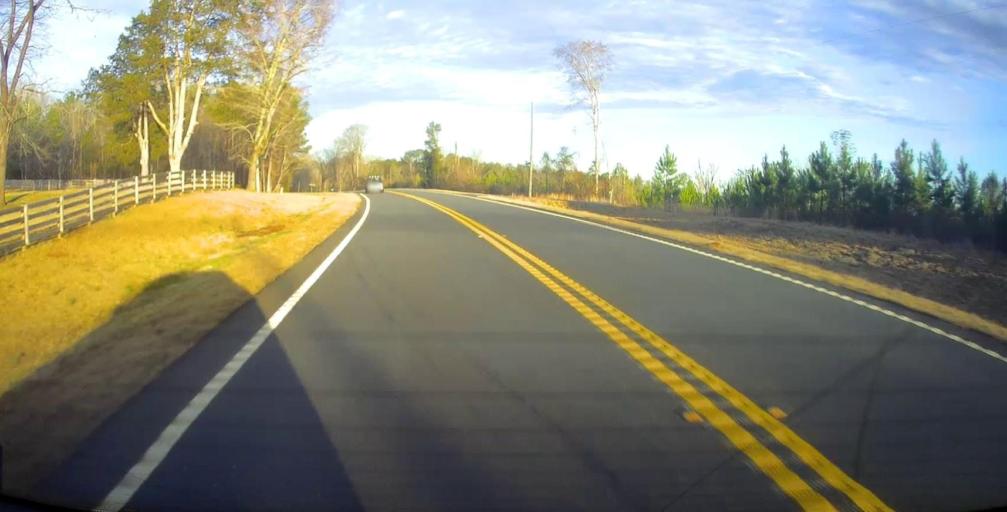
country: US
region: Georgia
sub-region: Talbot County
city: Sardis
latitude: 32.7213
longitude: -84.6525
